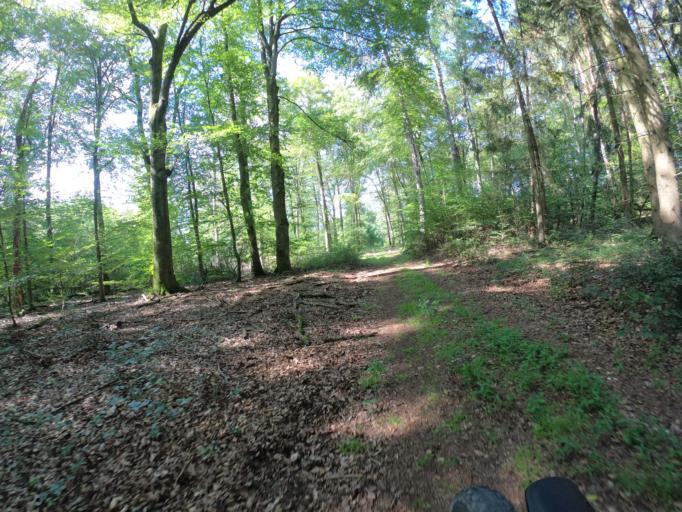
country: DE
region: Hesse
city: Morfelden-Walldorf
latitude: 49.9967
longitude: 8.6247
